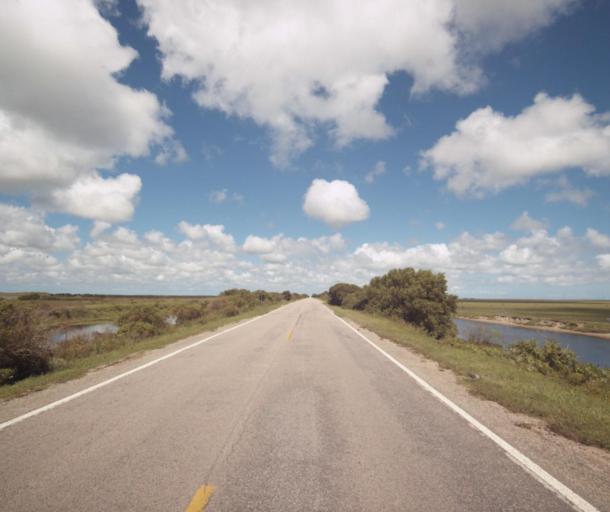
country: BR
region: Rio Grande do Sul
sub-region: Arroio Grande
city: Arroio Grande
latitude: -32.5433
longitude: -52.5415
